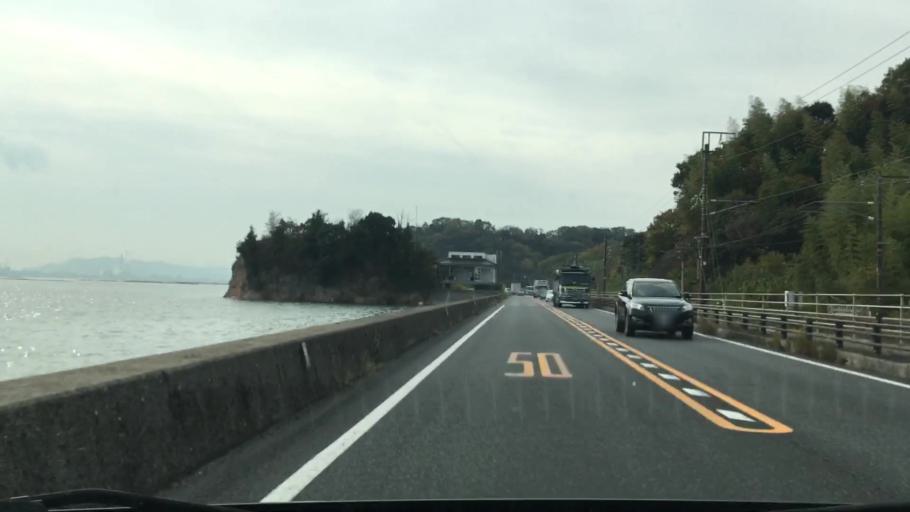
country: JP
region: Hiroshima
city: Ono-hara
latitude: 34.2689
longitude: 132.2523
